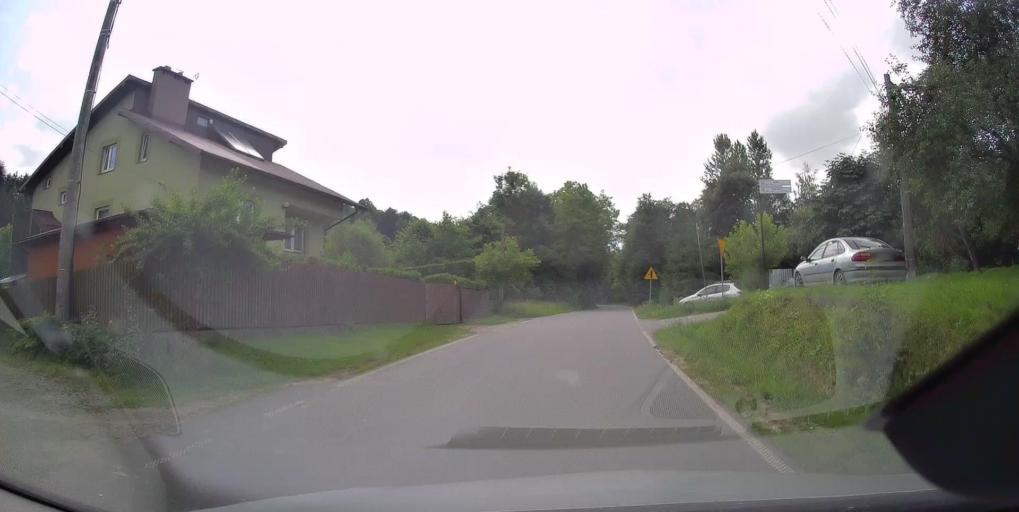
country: PL
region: Lesser Poland Voivodeship
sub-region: Powiat nowosadecki
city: Korzenna
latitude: 49.7265
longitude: 20.7731
